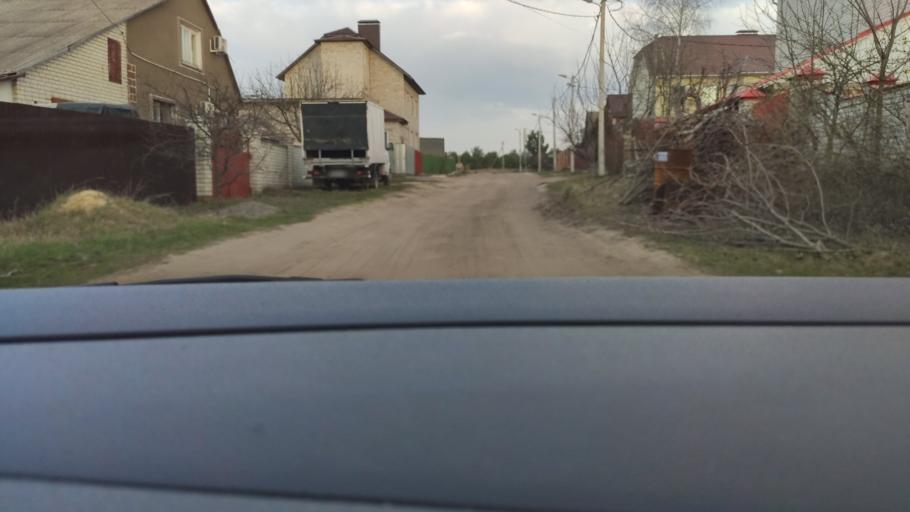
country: RU
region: Voronezj
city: Pridonskoy
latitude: 51.6293
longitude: 39.0927
